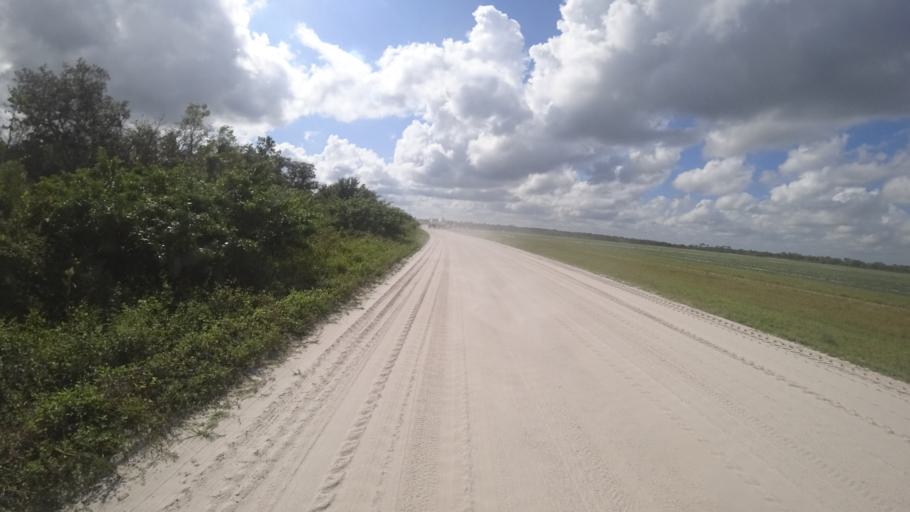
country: US
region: Florida
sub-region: Sarasota County
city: Lake Sarasota
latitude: 27.4174
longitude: -82.1888
